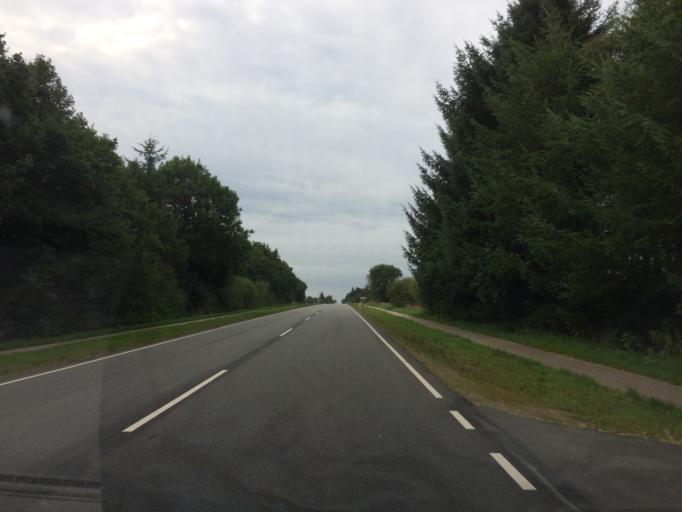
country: DK
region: Central Jutland
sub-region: Herning Kommune
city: Lind
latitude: 56.0781
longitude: 8.9847
